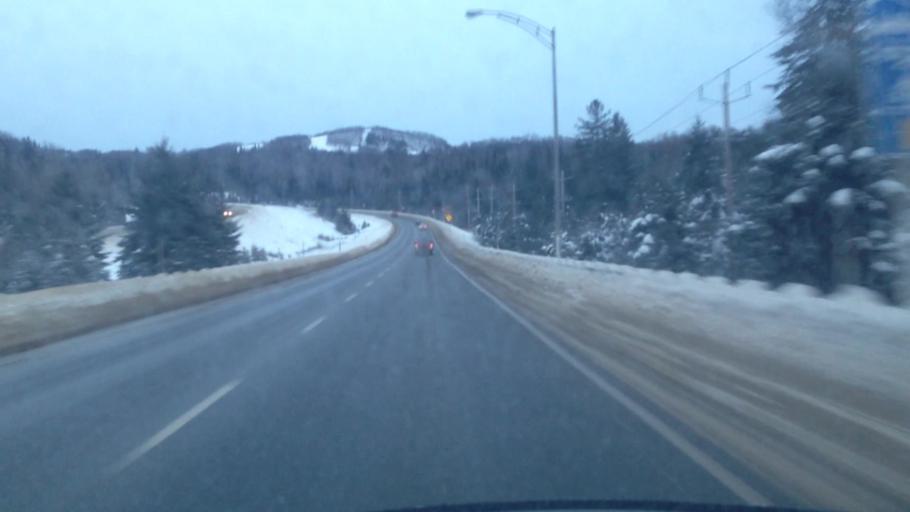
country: CA
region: Quebec
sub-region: Laurentides
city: Mont-Tremblant
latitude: 46.1112
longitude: -74.5168
